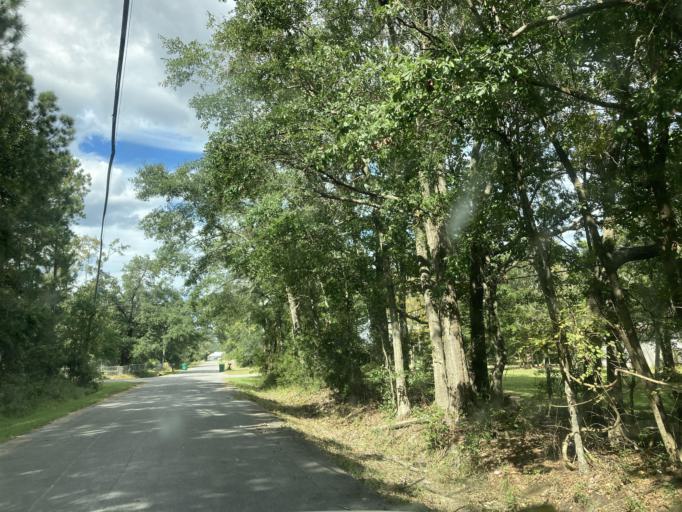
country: US
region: Mississippi
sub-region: Jackson County
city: Saint Martin
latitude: 30.4370
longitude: -88.8737
